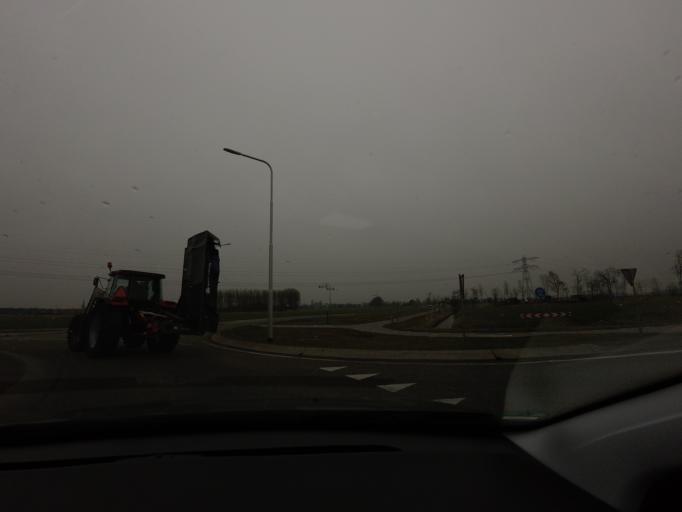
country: NL
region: Friesland
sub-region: Gemeente Franekeradeel
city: Franeker
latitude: 53.1741
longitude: 5.5513
